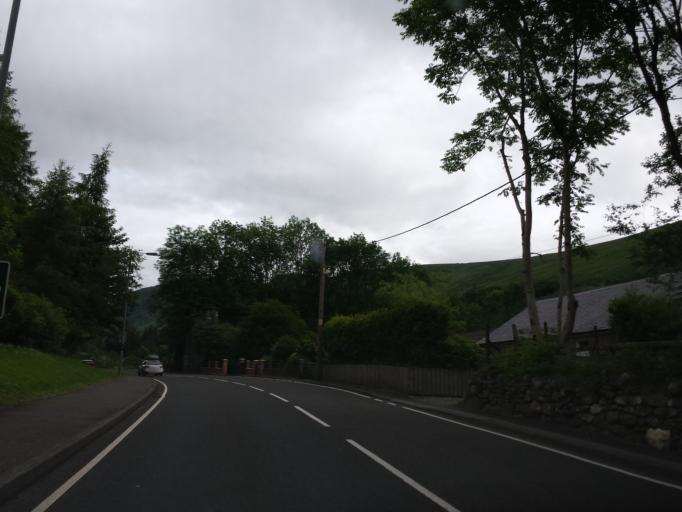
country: GB
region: Scotland
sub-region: Stirling
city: Callander
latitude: 56.3865
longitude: -4.2880
